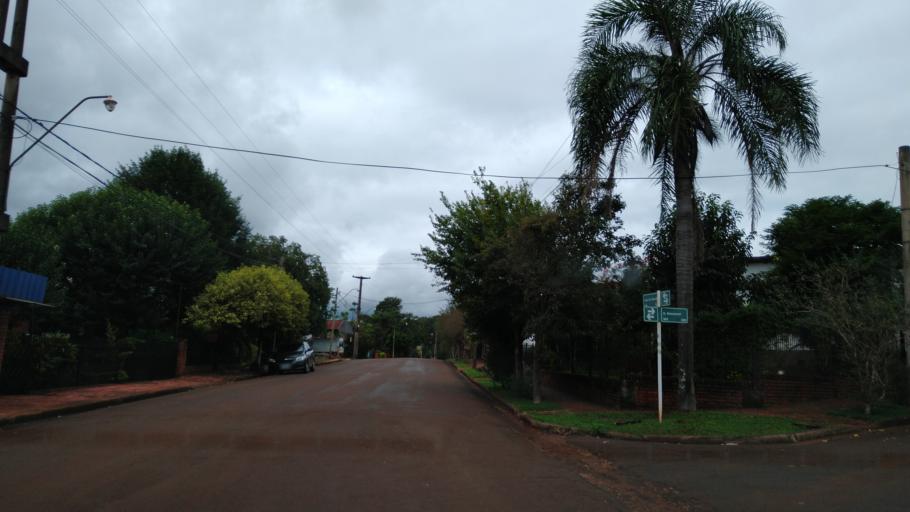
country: AR
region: Misiones
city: Capiovi
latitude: -26.9268
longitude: -55.0569
